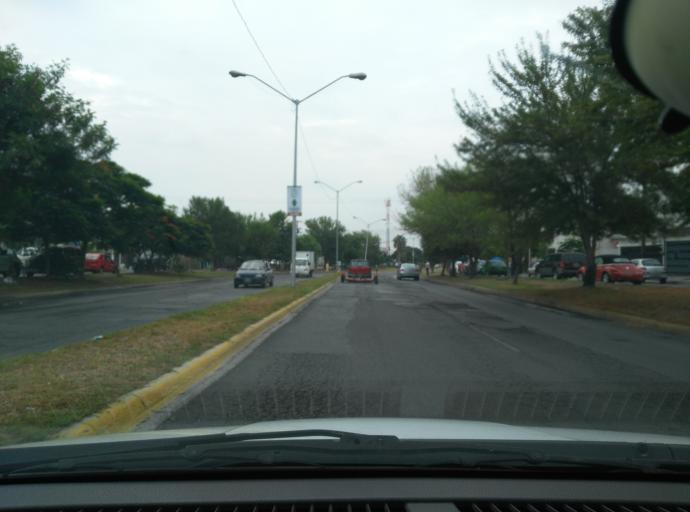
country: MX
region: Nuevo Leon
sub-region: Apodaca
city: Fraccionamiento Cosmopolis Octavo Sector
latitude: 25.7712
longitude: -100.2514
